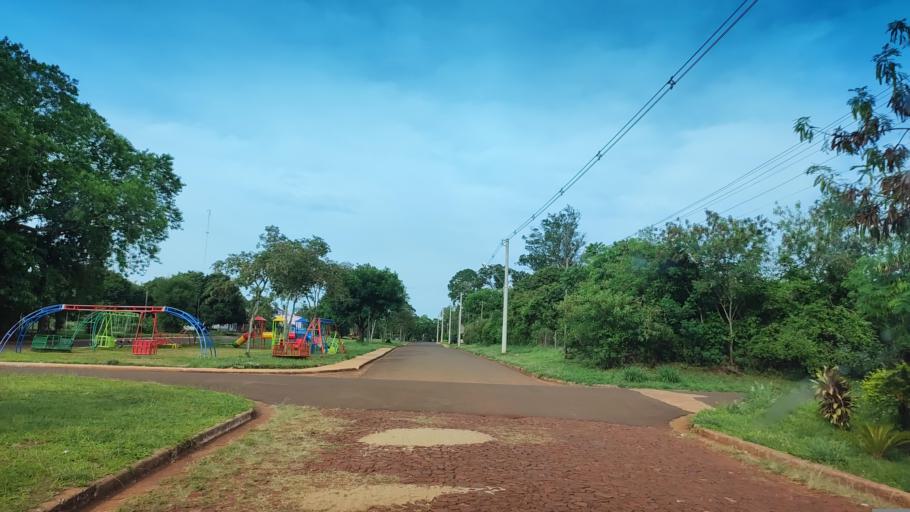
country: AR
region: Misiones
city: Gobernador Roca
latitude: -27.1321
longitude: -55.5136
